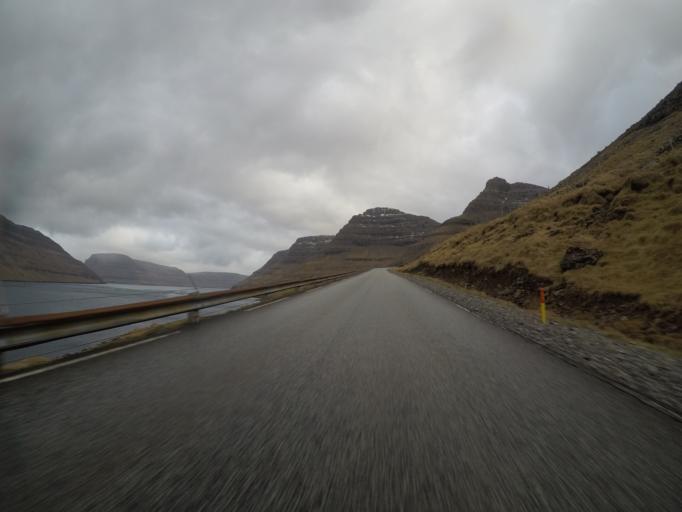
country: FO
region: Nordoyar
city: Klaksvik
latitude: 62.2809
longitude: -6.5254
